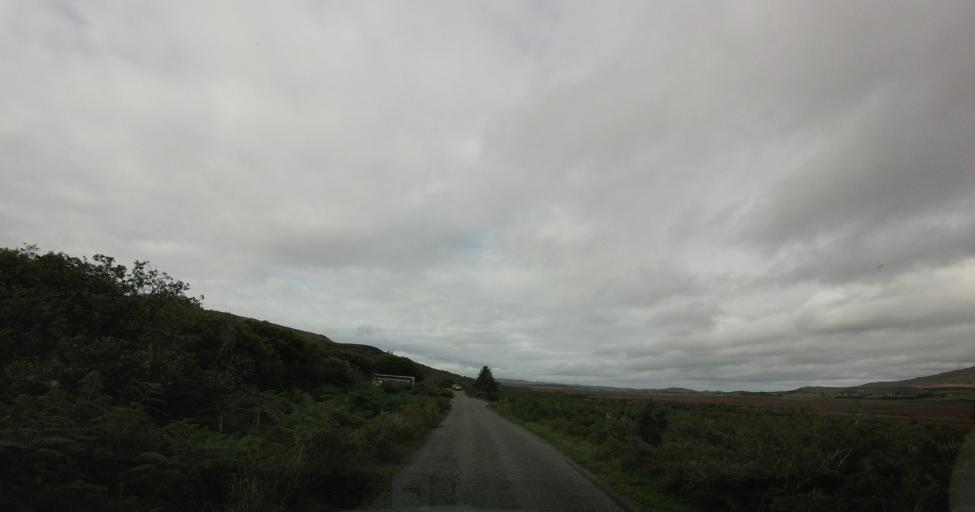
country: GB
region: Scotland
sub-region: Highland
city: Portree
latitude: 57.4167
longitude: -6.2264
